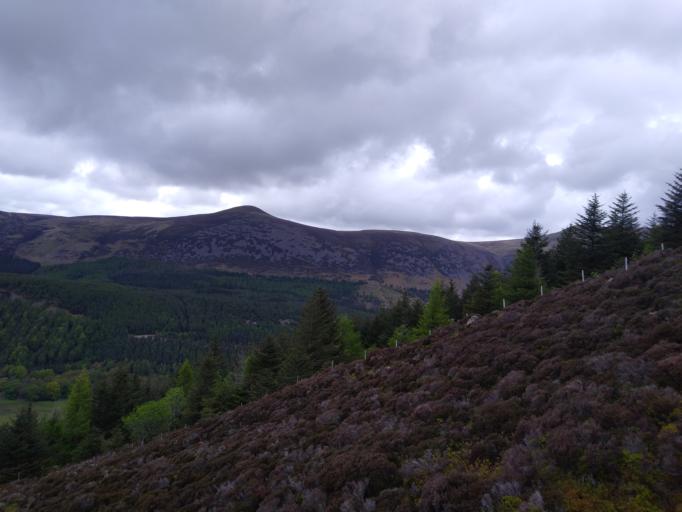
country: GB
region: England
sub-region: Cumbria
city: Cockermouth
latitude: 54.5074
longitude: -3.3364
